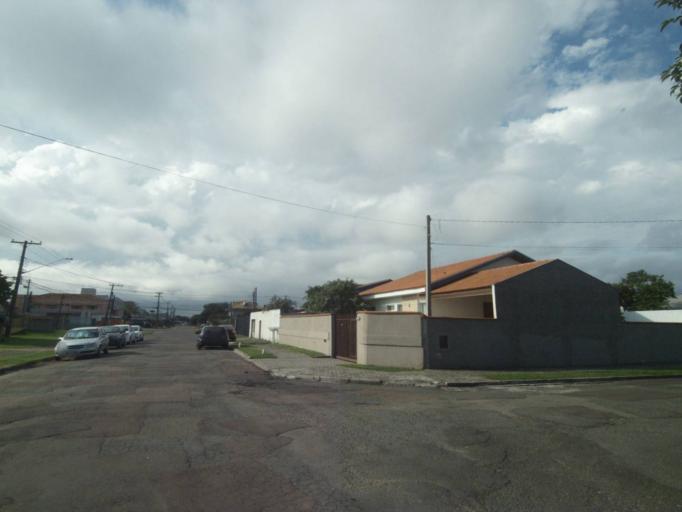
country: BR
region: Parana
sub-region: Pinhais
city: Pinhais
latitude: -25.4608
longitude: -49.2041
